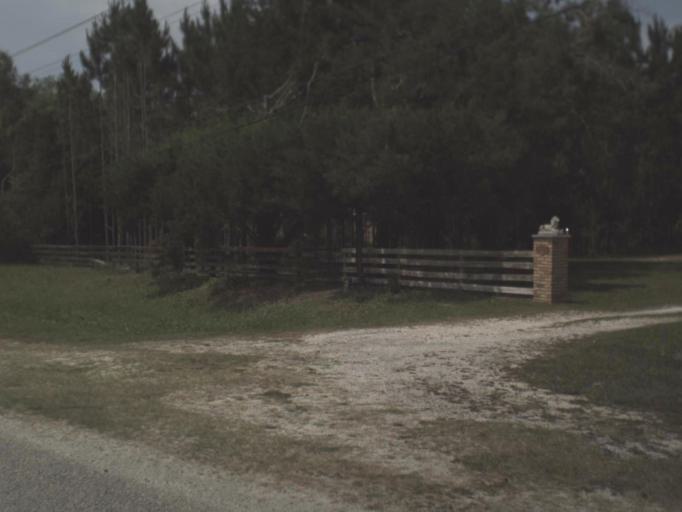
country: US
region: Florida
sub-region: Clay County
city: Green Cove Springs
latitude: 29.9315
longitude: -81.6876
